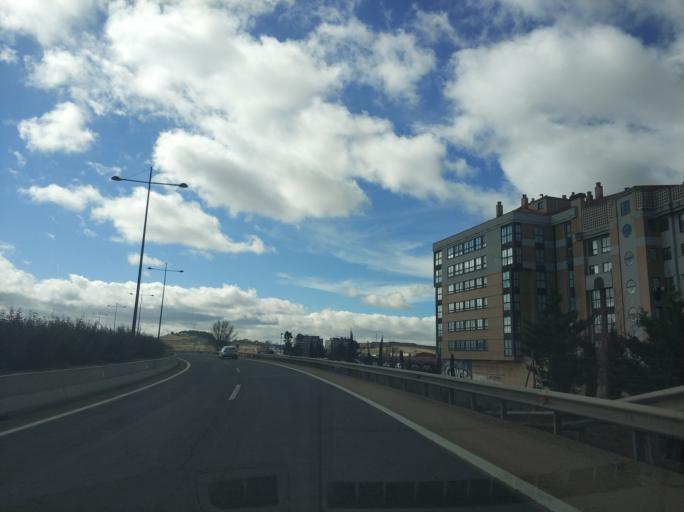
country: ES
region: Castille and Leon
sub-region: Provincia de Burgos
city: Burgos
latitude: 42.3323
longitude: -3.6967
